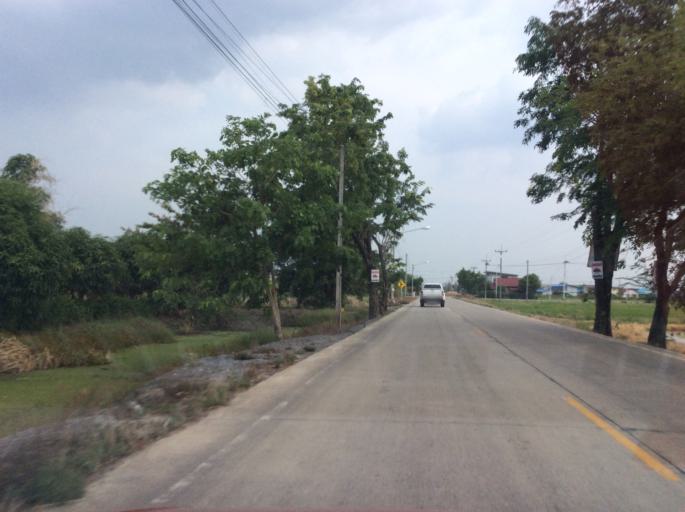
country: TH
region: Pathum Thani
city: Lam Luk Ka
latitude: 13.9712
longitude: 100.7262
